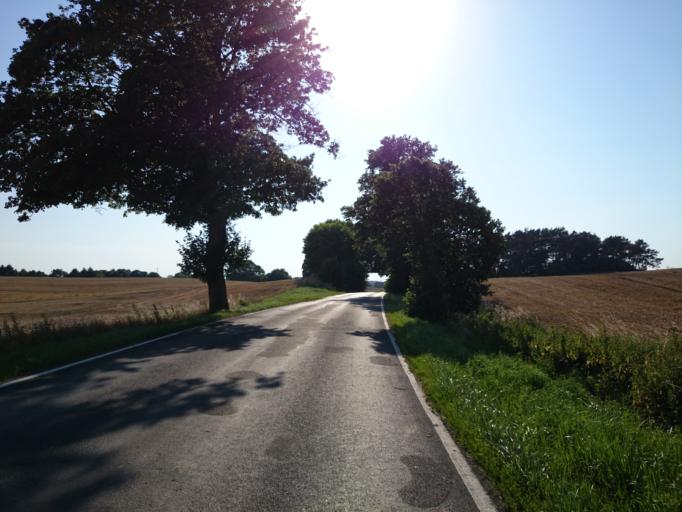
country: DE
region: Mecklenburg-Vorpommern
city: Tessin
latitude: 54.0228
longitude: 12.4462
